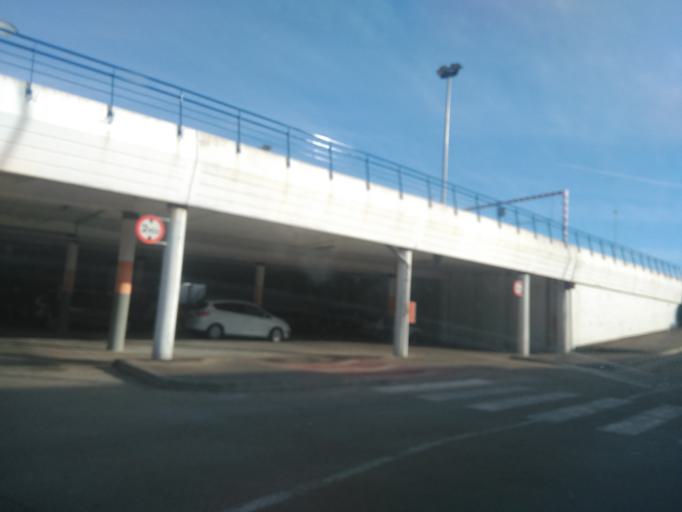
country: ES
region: Castille and Leon
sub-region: Provincia de Salamanca
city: Santa Marta de Tormes
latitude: 40.9464
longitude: -5.6405
